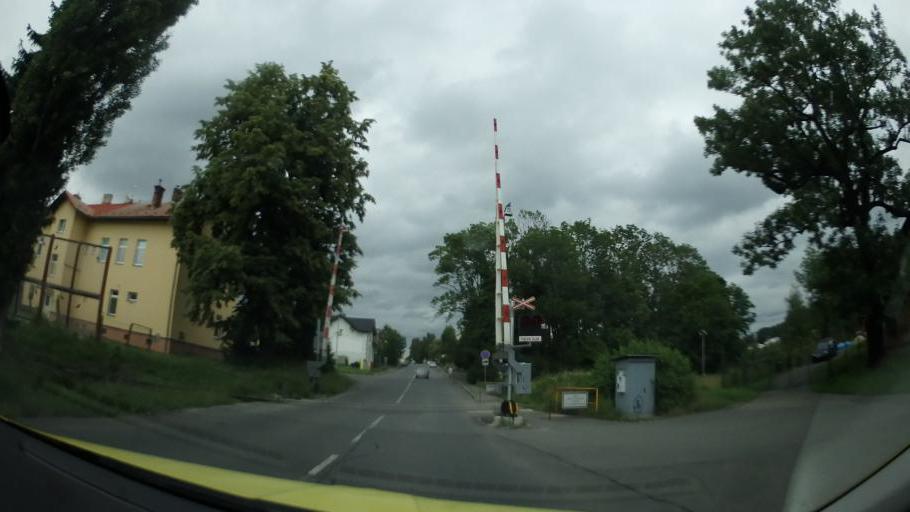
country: CZ
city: Stramberk
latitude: 49.5822
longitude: 18.1281
